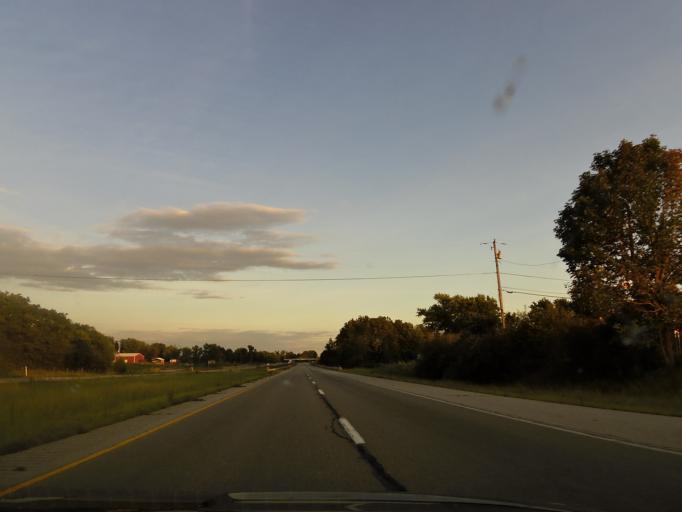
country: US
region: Indiana
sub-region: Hancock County
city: New Palestine
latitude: 39.6134
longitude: -85.8629
